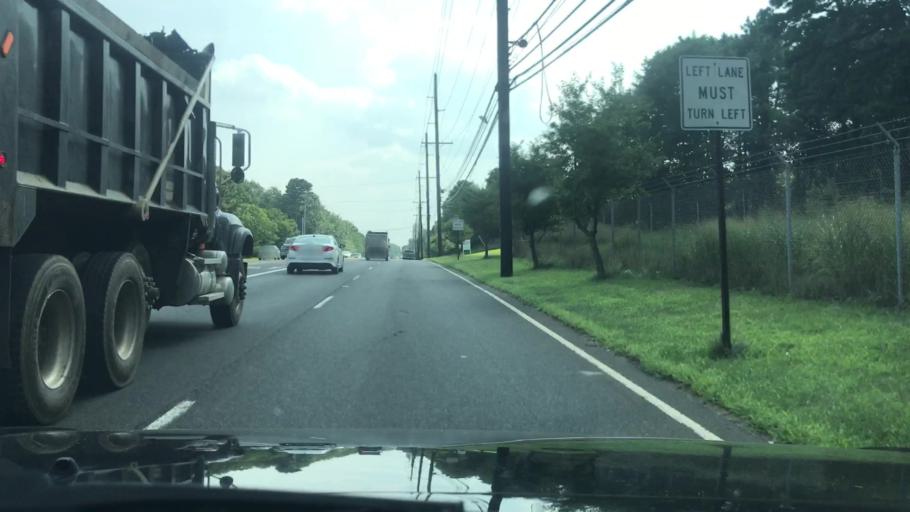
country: US
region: New Jersey
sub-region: Monmouth County
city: Tinton Falls
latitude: 40.2507
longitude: -74.0976
